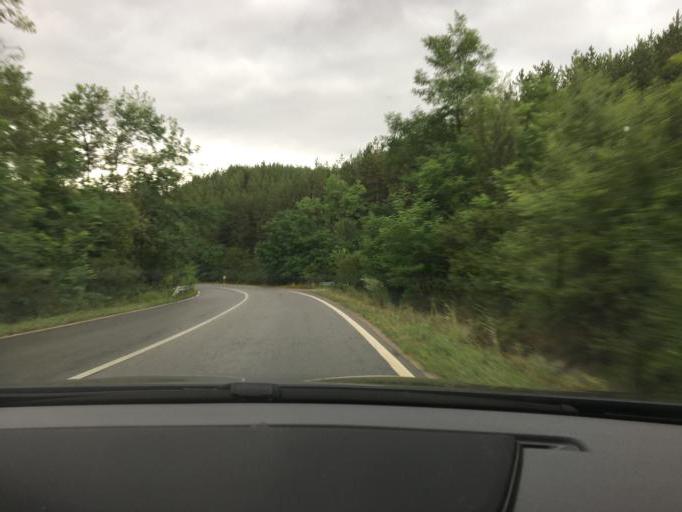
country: BG
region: Kyustendil
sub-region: Obshtina Boboshevo
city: Boboshevo
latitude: 42.2545
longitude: 22.8860
